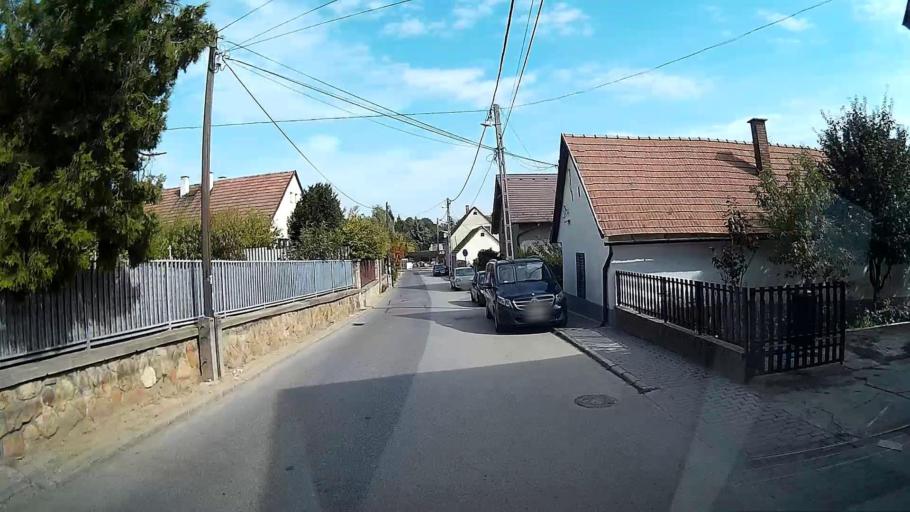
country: HU
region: Pest
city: Solymar
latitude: 47.5892
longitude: 18.9348
